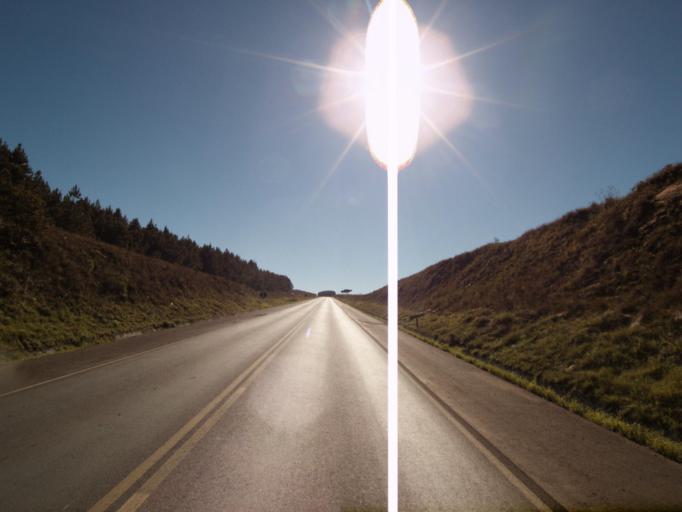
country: BR
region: Parana
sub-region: Palmas
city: Palmas
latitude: -26.7584
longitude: -51.6658
